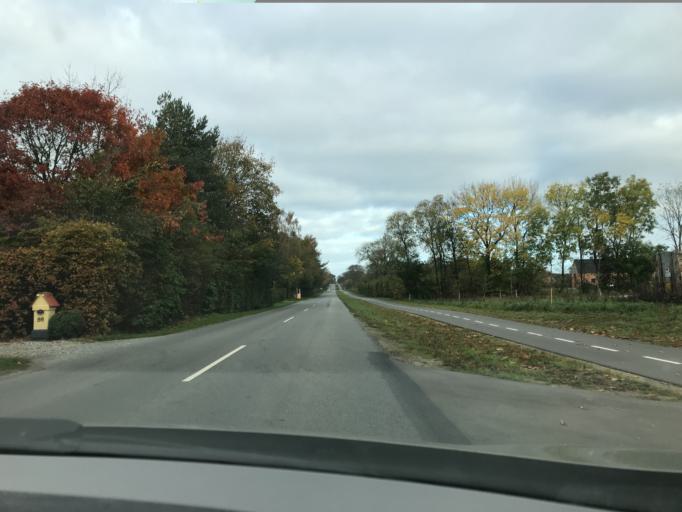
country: DK
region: South Denmark
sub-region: Kolding Kommune
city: Kolding
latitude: 55.5475
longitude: 9.4137
